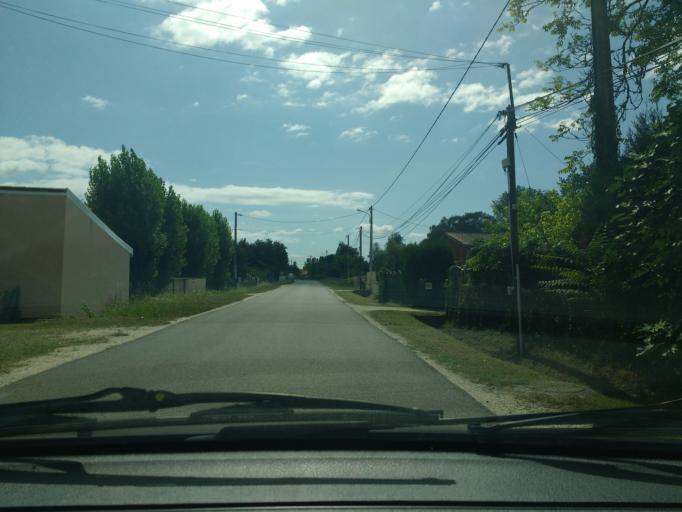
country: FR
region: Aquitaine
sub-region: Departement de la Gironde
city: Salles
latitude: 44.5606
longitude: -0.8501
